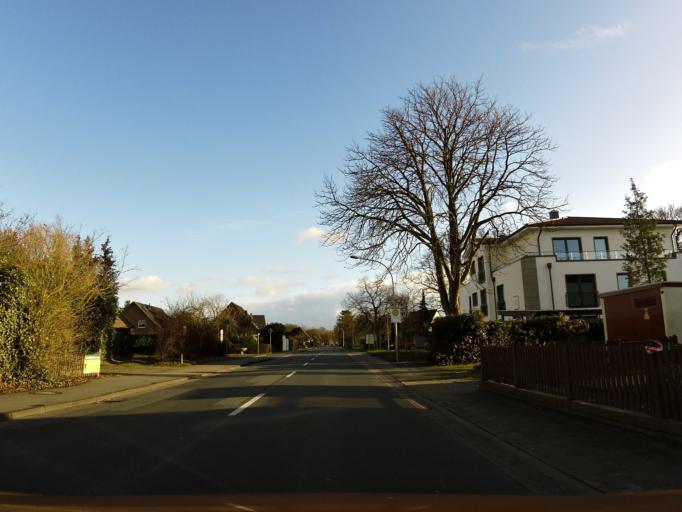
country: DE
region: Lower Saxony
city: Verden
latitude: 52.9068
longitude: 9.2697
